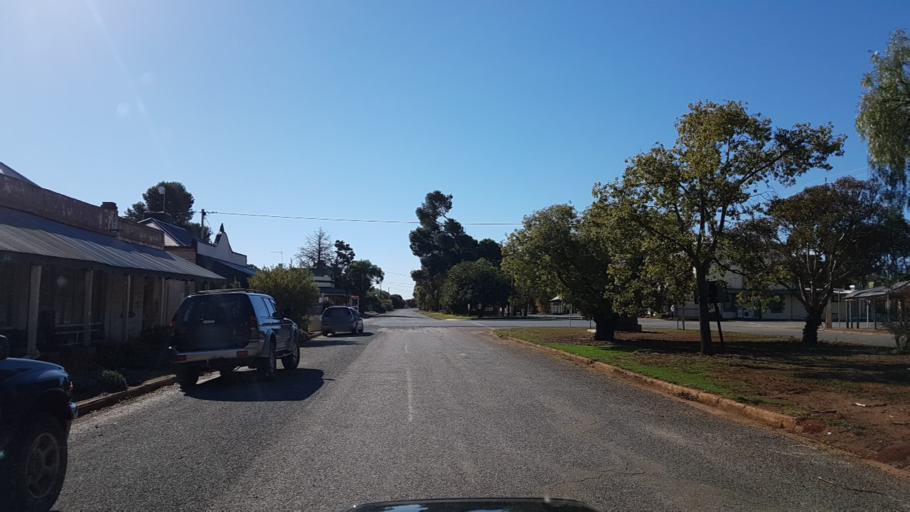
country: AU
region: South Australia
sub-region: Peterborough
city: Peterborough
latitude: -33.0300
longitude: 138.7497
